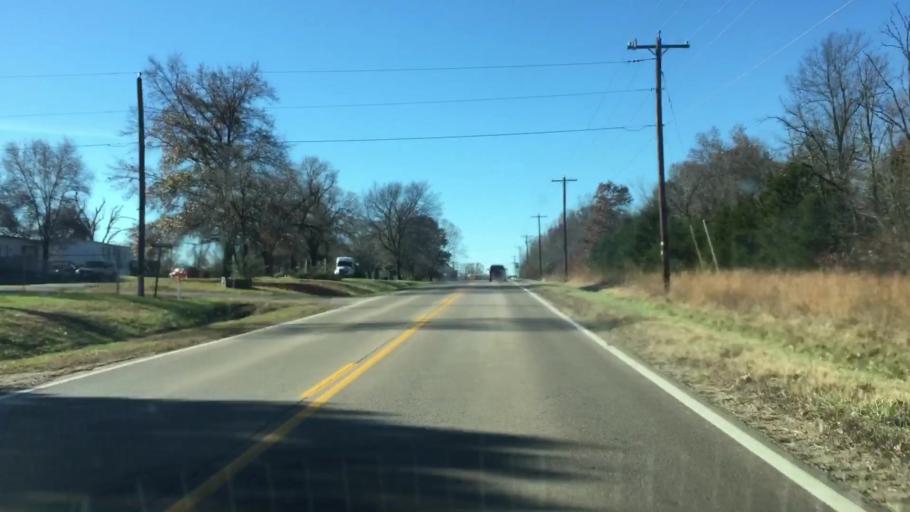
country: US
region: Missouri
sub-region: Miller County
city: Eldon
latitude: 38.3592
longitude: -92.5633
